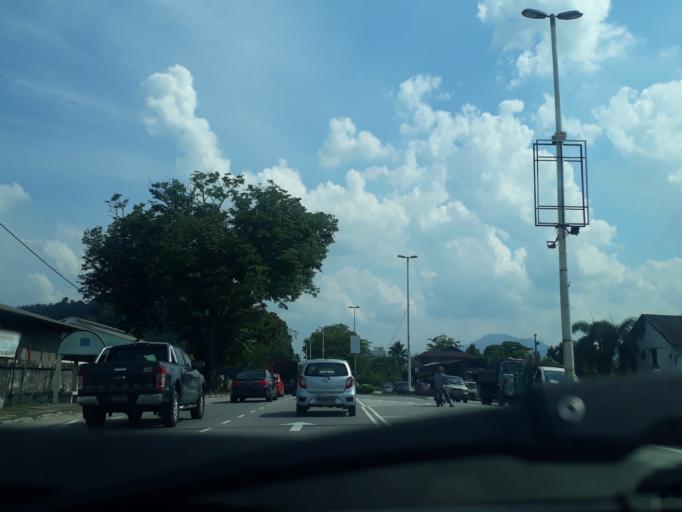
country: MY
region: Perak
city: Ipoh
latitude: 4.6492
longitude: 101.1034
